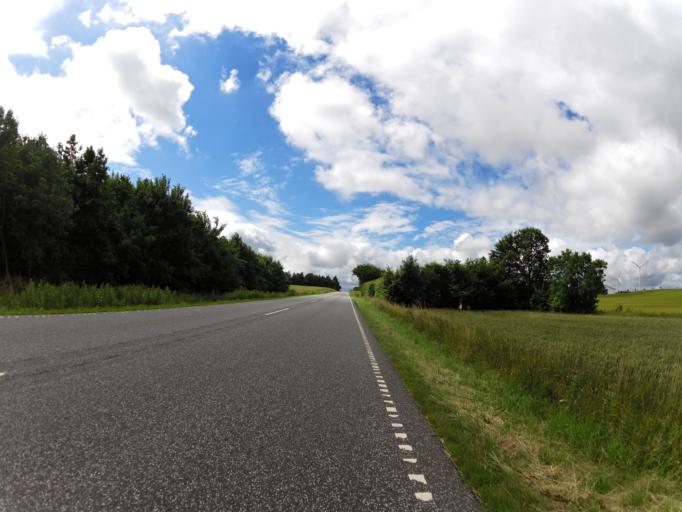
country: DK
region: North Denmark
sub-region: Mariagerfjord Kommune
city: Hadsund
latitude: 56.6007
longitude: 10.1408
